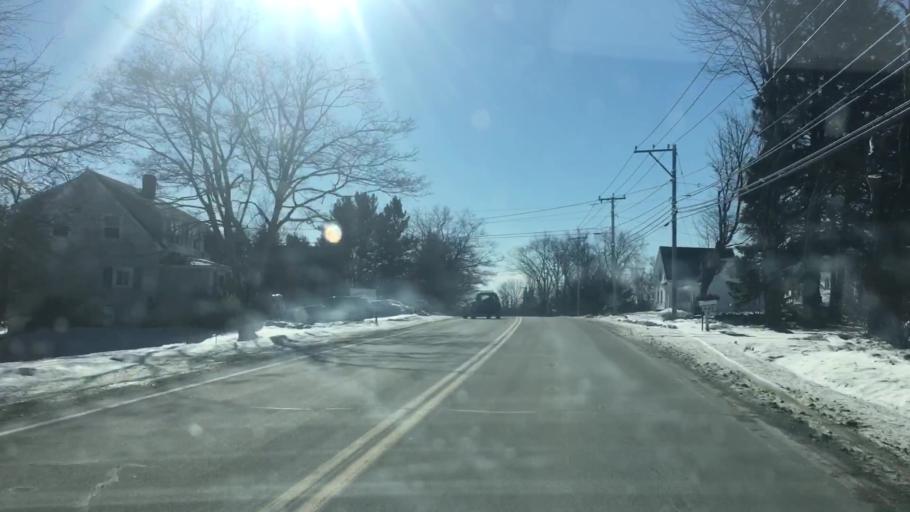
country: US
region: Maine
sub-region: Hancock County
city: Ellsworth
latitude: 44.5102
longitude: -68.4378
